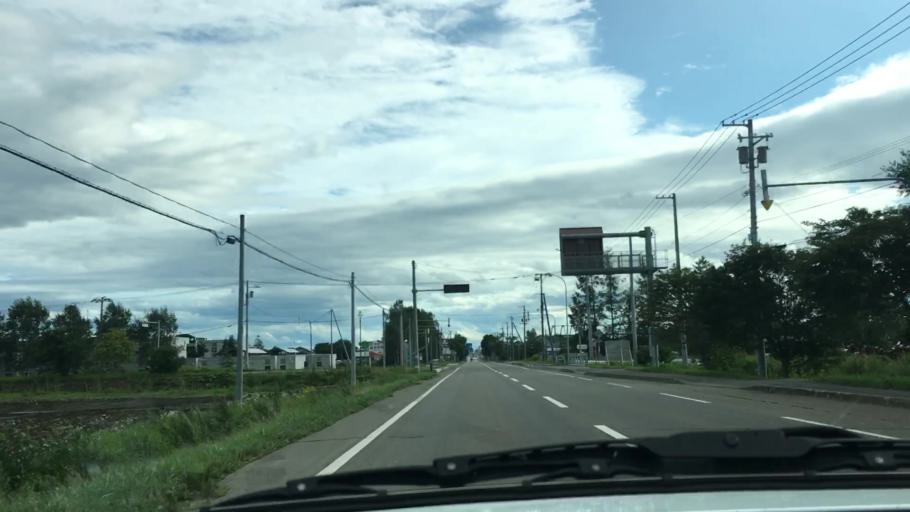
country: JP
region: Hokkaido
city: Otofuke
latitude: 43.2405
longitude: 143.2968
